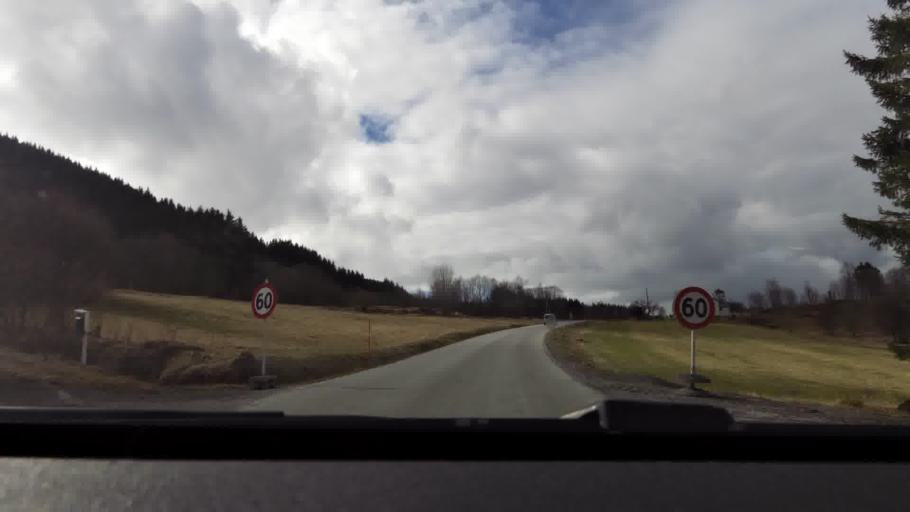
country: NO
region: More og Romsdal
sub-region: Gjemnes
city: Batnfjordsora
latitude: 62.9560
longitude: 7.6648
